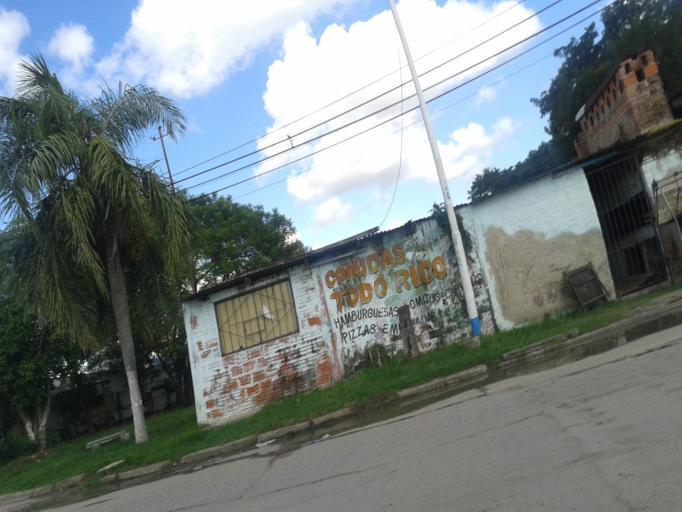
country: AR
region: Formosa
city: Clorinda
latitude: -25.2828
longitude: -57.7382
